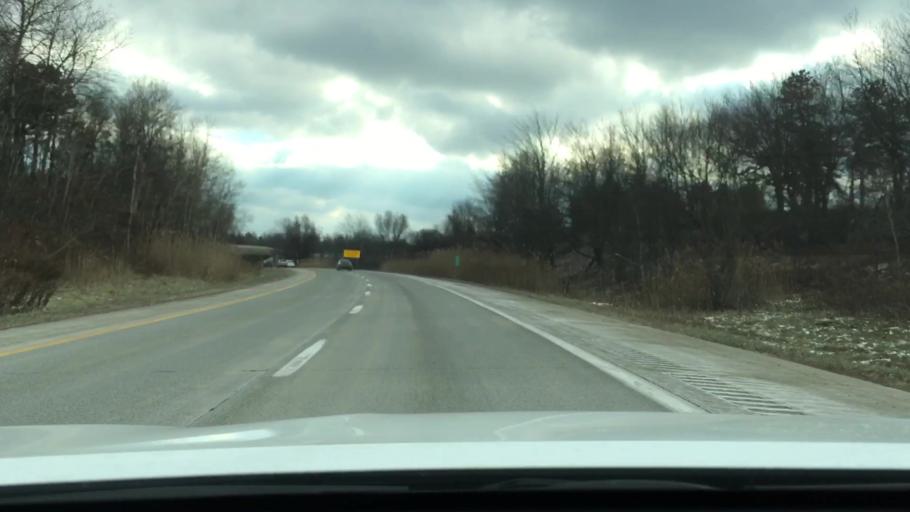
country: US
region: Pennsylvania
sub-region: Monroe County
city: Emerald Lakes
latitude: 41.0731
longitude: -75.3969
